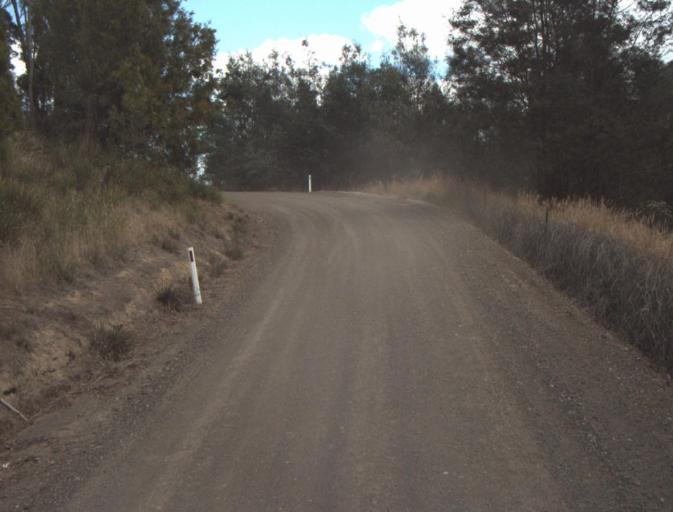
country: AU
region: Tasmania
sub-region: Launceston
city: Mayfield
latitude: -41.2177
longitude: 147.1685
